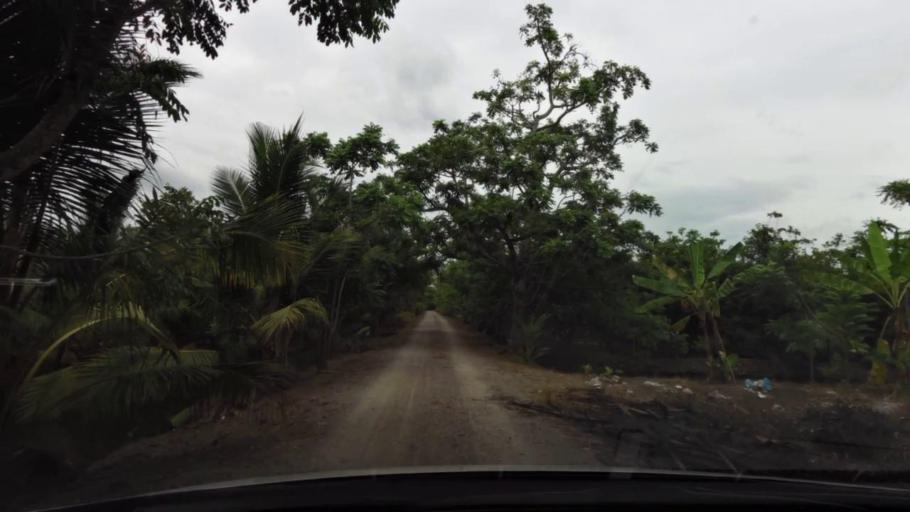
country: TH
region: Ratchaburi
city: Damnoen Saduak
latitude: 13.5650
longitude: 100.0044
